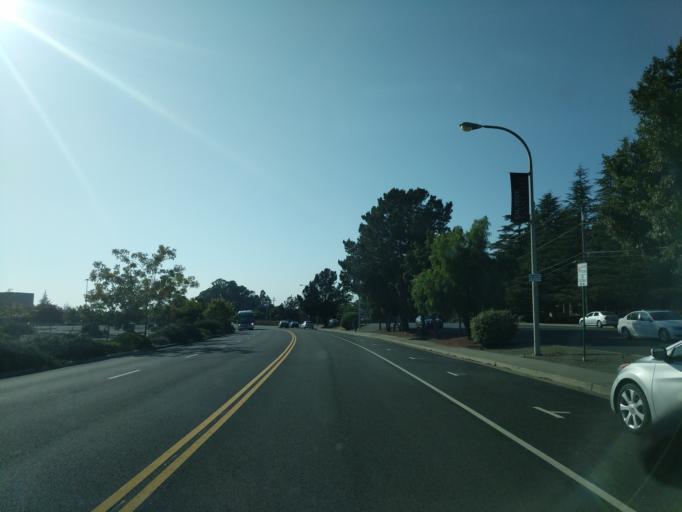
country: US
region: California
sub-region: Alameda County
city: Fairview
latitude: 37.6594
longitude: -122.0529
